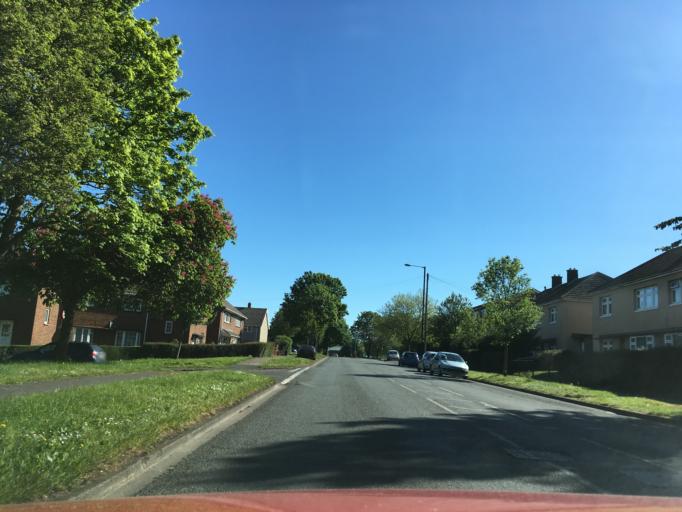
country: GB
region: England
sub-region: North Somerset
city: Easton-in-Gordano
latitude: 51.5007
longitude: -2.6619
